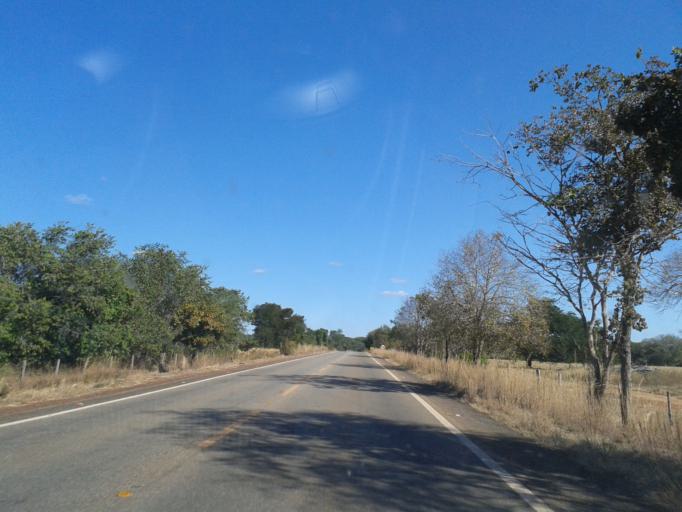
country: BR
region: Goias
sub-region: Mozarlandia
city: Mozarlandia
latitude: -14.3030
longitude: -50.4040
